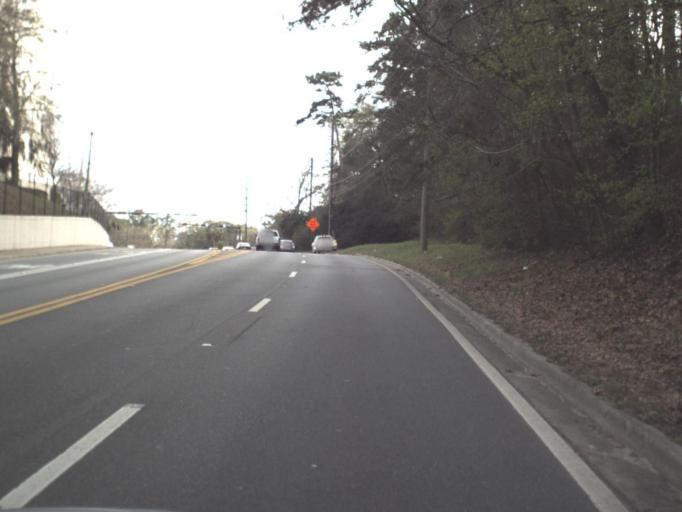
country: US
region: Florida
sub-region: Leon County
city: Tallahassee
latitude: 30.4586
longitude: -84.2626
